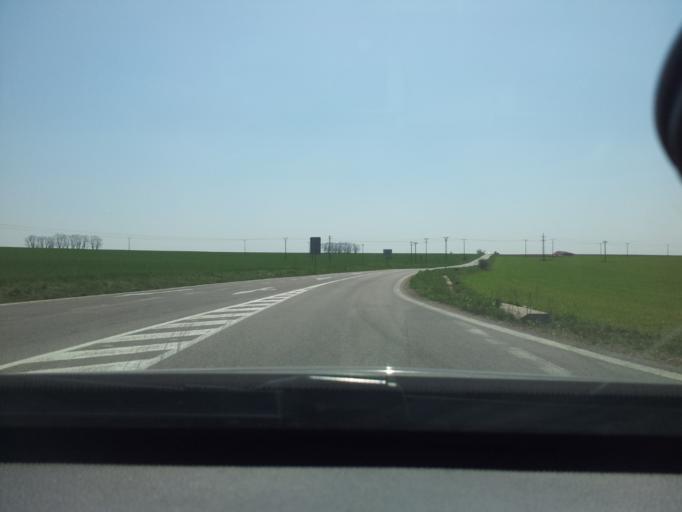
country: SK
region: Nitriansky
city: Zlate Moravce
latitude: 48.3737
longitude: 18.4052
